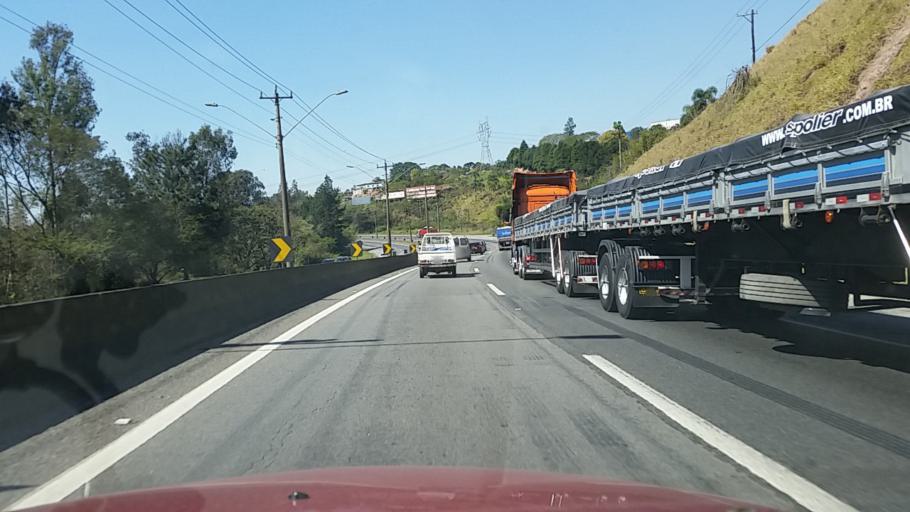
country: BR
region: Sao Paulo
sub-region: Itapecerica Da Serra
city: Itapecerica da Serra
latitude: -23.7227
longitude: -46.8904
